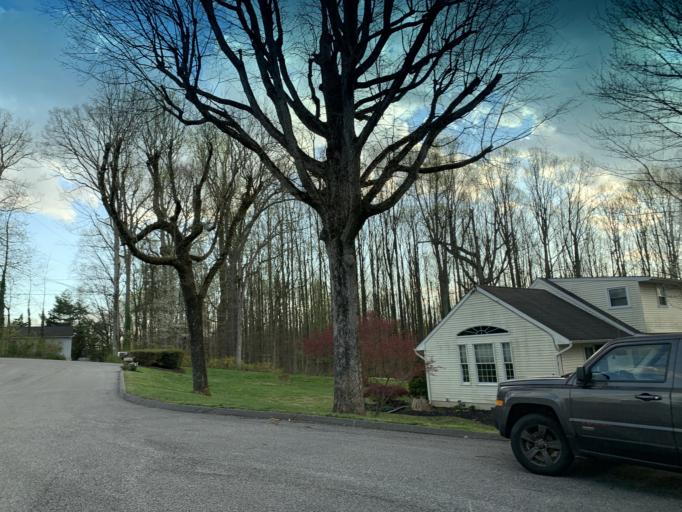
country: US
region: Maryland
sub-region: Harford County
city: South Bel Air
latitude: 39.5999
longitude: -76.3218
